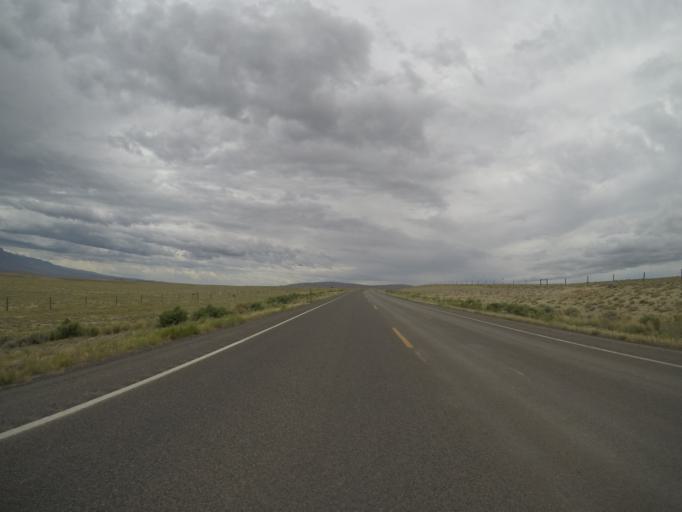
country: US
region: Wyoming
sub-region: Big Horn County
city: Lovell
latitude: 44.8932
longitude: -108.2887
